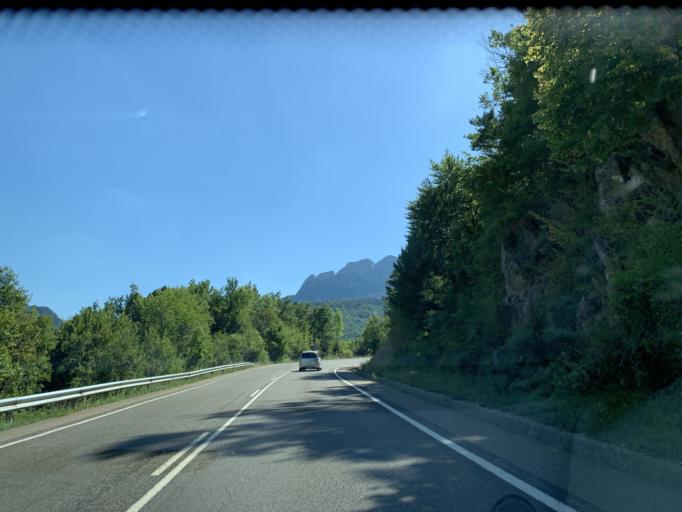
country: ES
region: Aragon
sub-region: Provincia de Huesca
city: Hoz de Jaca
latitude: 42.7083
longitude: -0.3117
